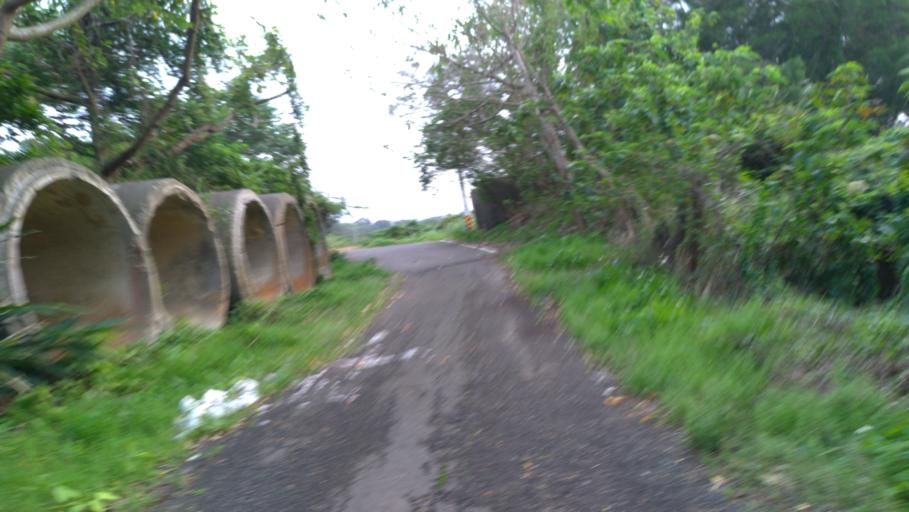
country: TW
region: Taiwan
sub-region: Hsinchu
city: Hsinchu
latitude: 24.7518
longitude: 120.9848
